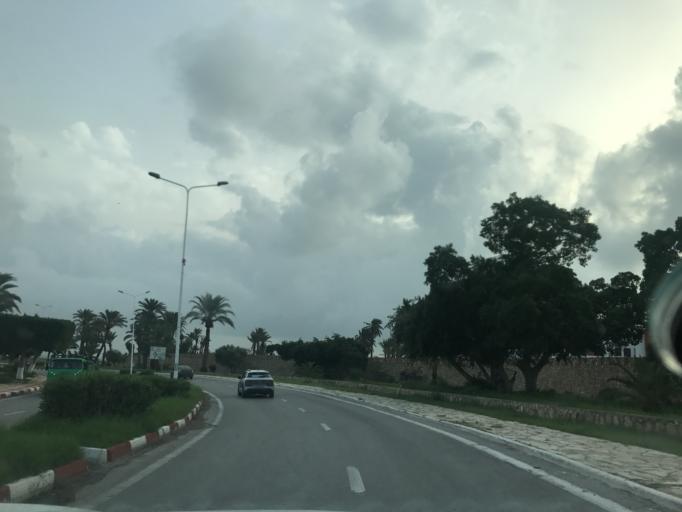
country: TN
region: Al Munastir
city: Saqanis
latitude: 35.7762
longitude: 10.7841
